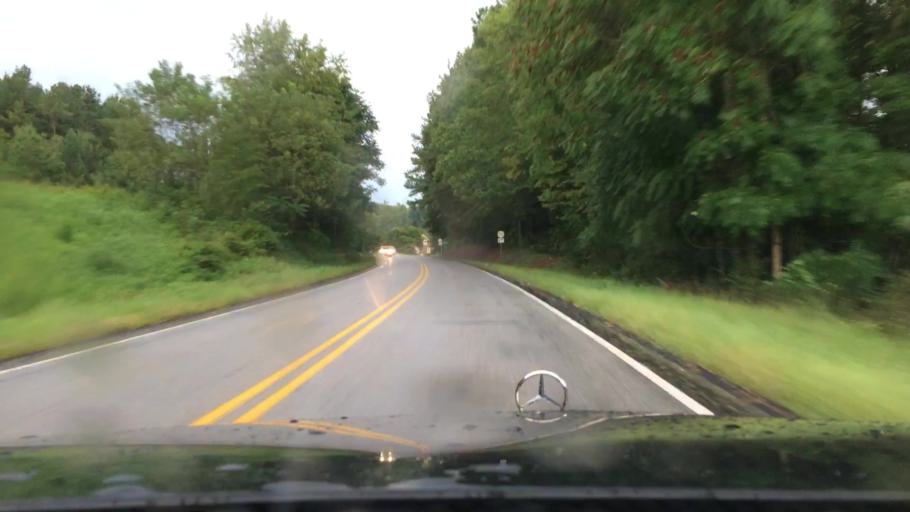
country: US
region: Virginia
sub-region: Amherst County
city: Amherst
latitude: 37.6973
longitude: -79.0297
